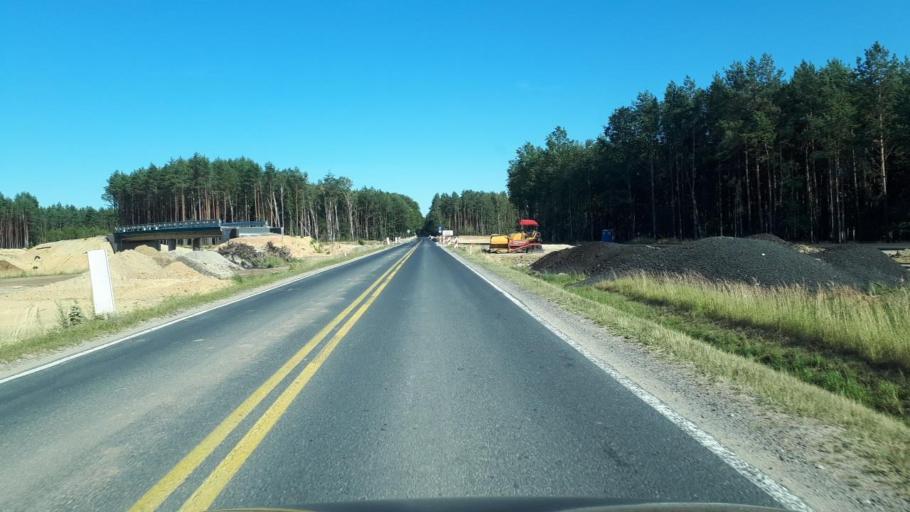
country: PL
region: Silesian Voivodeship
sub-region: Powiat lubliniecki
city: Sierakow Slaski
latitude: 50.8163
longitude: 18.5425
